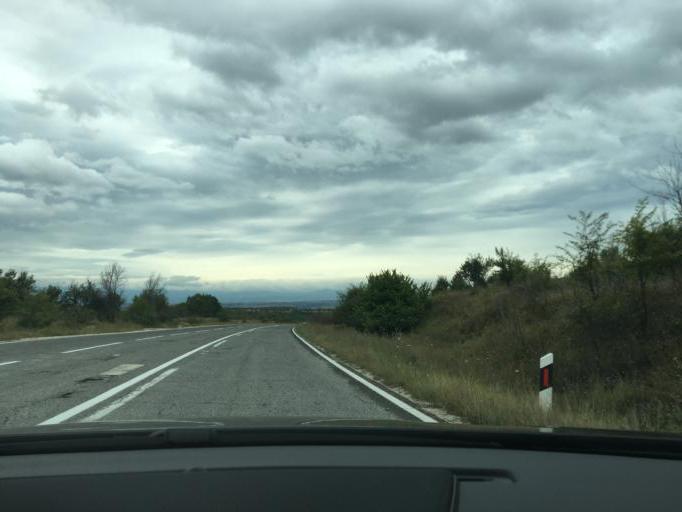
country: MK
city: Klechovce
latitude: 42.1494
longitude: 21.9659
